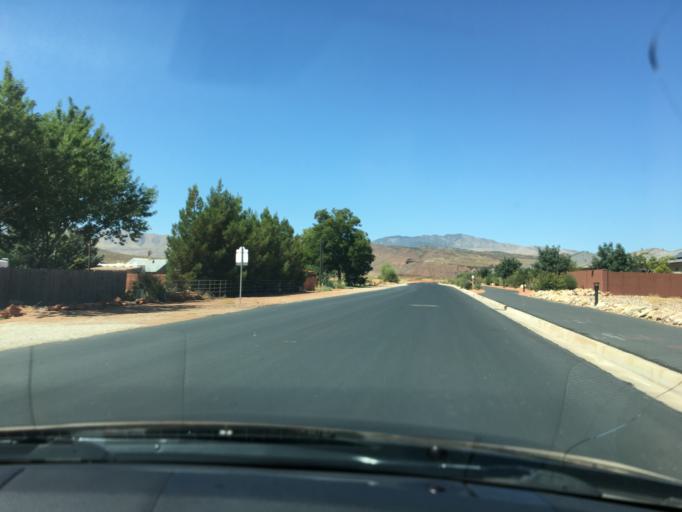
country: US
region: Utah
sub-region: Washington County
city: Ivins
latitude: 37.1609
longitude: -113.6888
